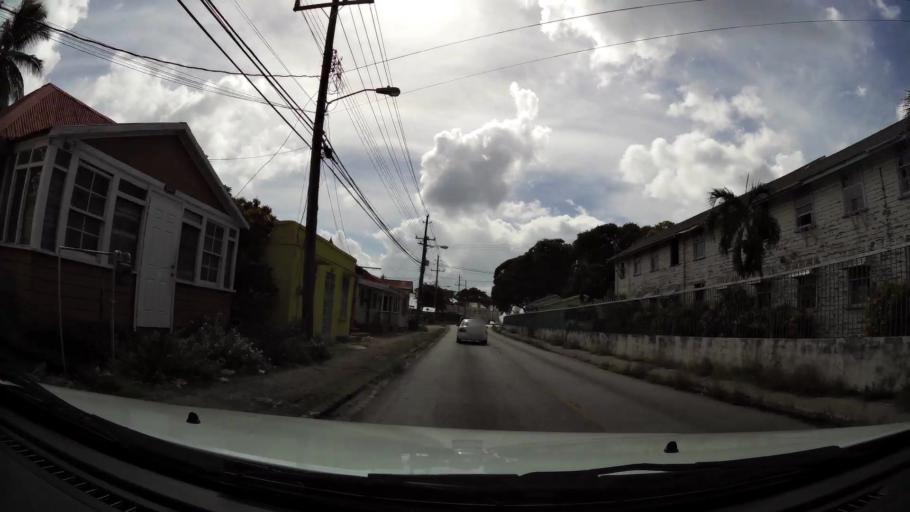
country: BB
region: Saint Michael
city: Bridgetown
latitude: 13.0928
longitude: -59.6084
